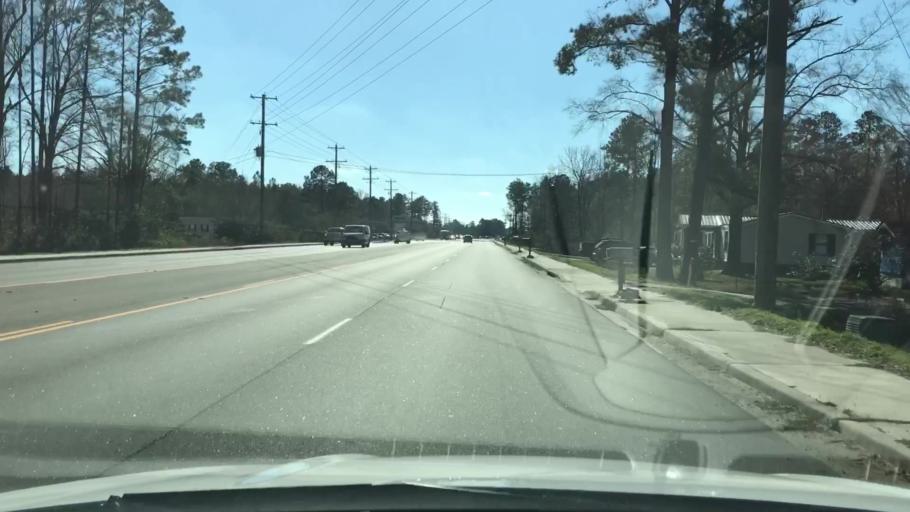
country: US
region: South Carolina
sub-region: Horry County
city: Garden City
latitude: 33.6365
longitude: -79.0332
